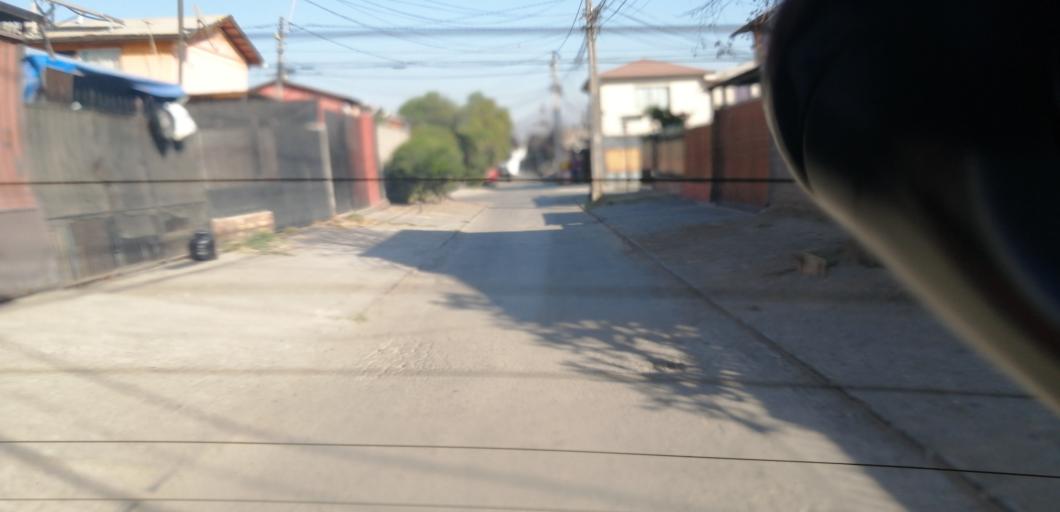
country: CL
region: Santiago Metropolitan
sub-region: Provincia de Santiago
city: Lo Prado
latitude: -33.4610
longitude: -70.7449
